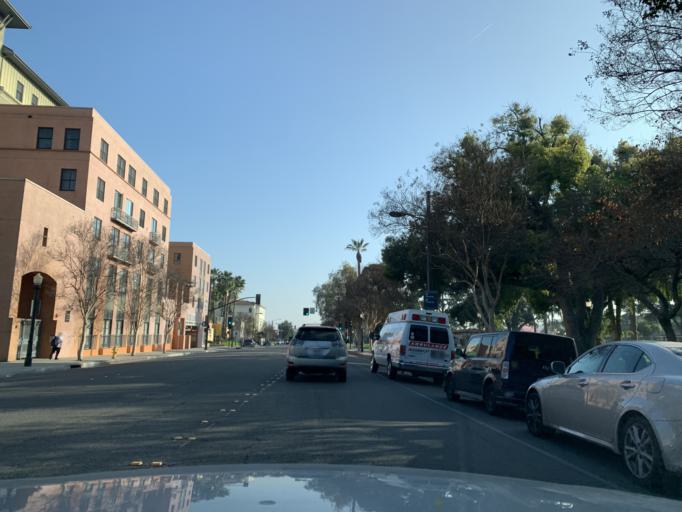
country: US
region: California
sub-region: Los Angeles County
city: Pasadena
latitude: 34.1426
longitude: -118.1489
